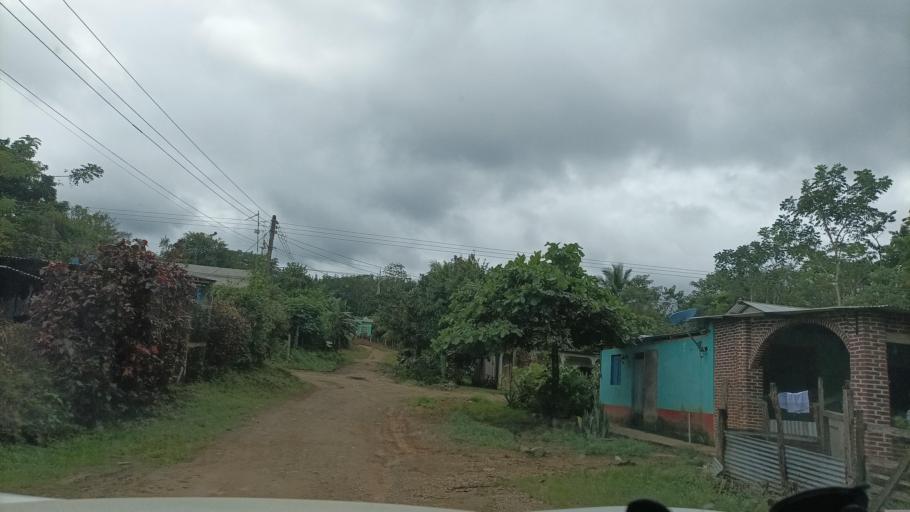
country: MX
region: Veracruz
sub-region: Uxpanapa
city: Poblado 10
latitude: 17.2690
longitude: -94.4996
